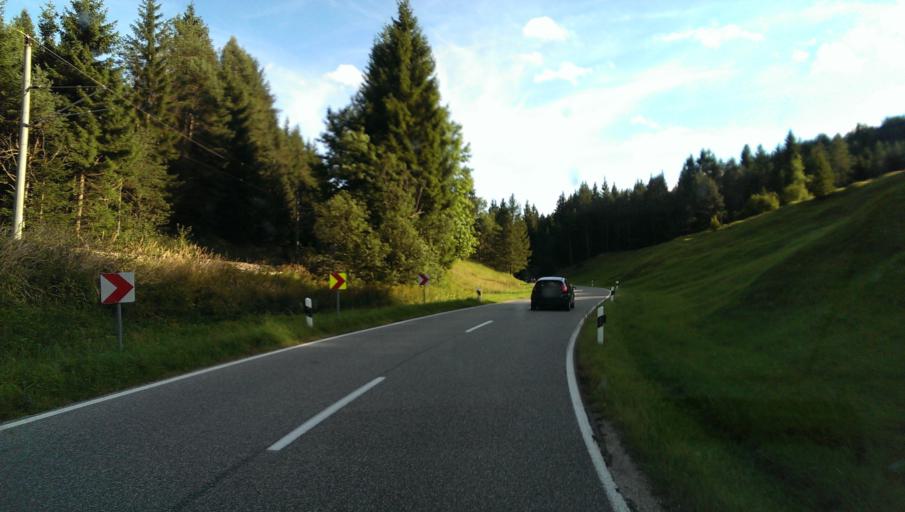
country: DE
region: Bavaria
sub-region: Upper Bavaria
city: Mittenwald
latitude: 47.4711
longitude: 11.2573
